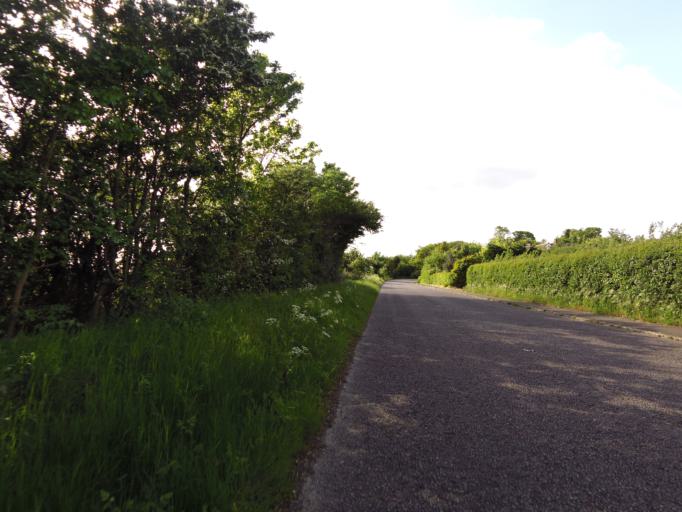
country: GB
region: England
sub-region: Suffolk
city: Beccles
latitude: 52.4492
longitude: 1.6107
